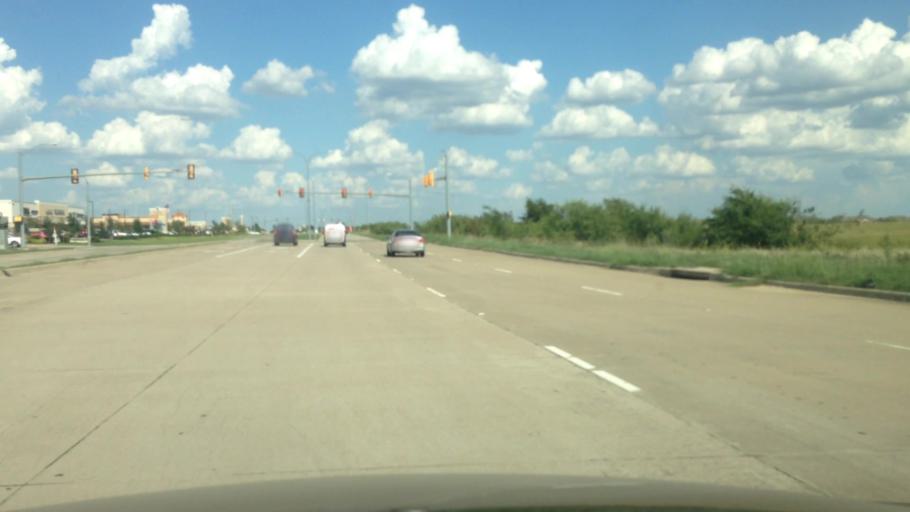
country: US
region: Texas
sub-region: Tarrant County
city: Blue Mound
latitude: 32.8984
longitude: -97.3267
